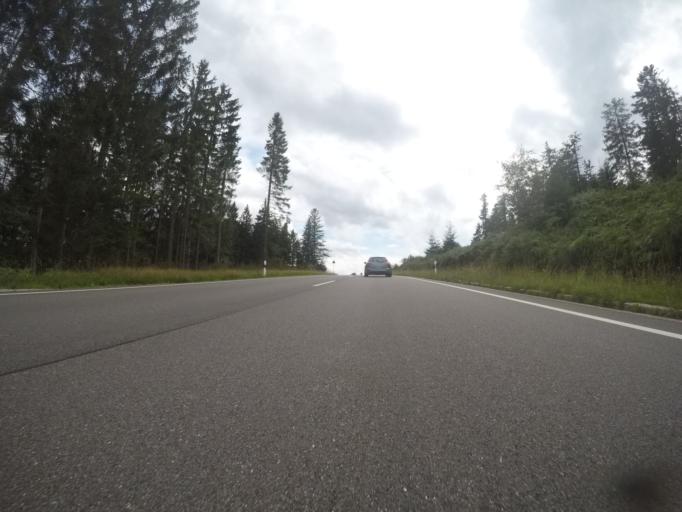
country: DE
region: Baden-Wuerttemberg
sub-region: Freiburg Region
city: Seebach
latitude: 48.5540
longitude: 8.2161
